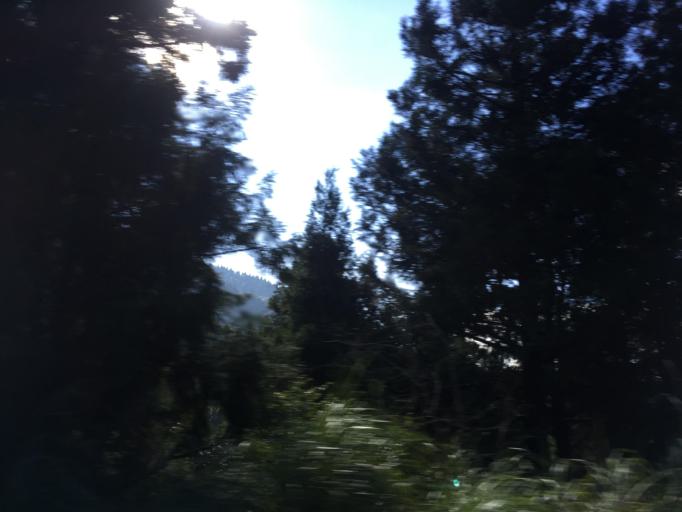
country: TW
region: Taiwan
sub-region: Yilan
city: Yilan
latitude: 24.5040
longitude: 121.5532
